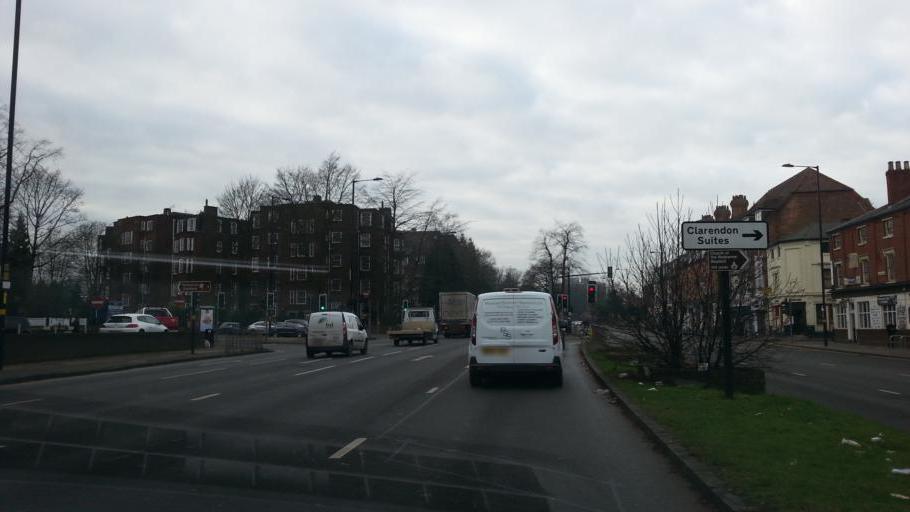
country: GB
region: England
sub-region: City and Borough of Birmingham
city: Hockley
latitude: 52.4718
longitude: -1.9305
